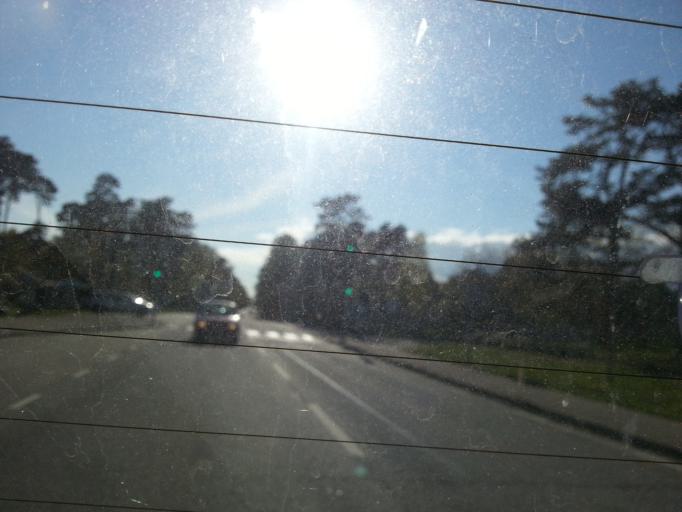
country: SE
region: Skane
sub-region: Ystads Kommun
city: Ystad
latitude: 55.4343
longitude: 13.8781
